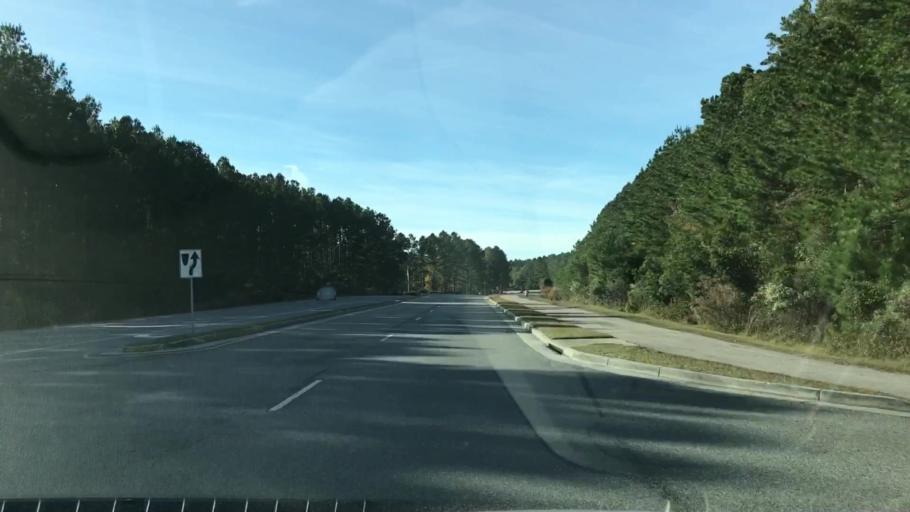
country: US
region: South Carolina
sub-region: Beaufort County
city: Bluffton
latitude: 32.2830
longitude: -80.9109
